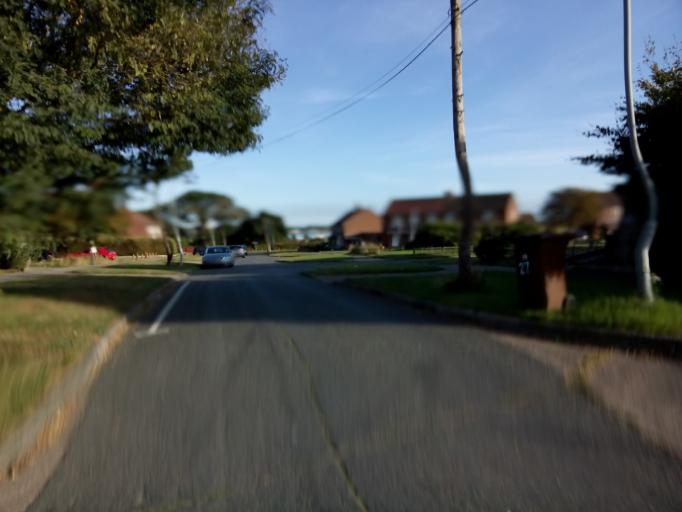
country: GB
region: England
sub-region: Suffolk
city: Ipswich
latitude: 52.0414
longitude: 1.1470
